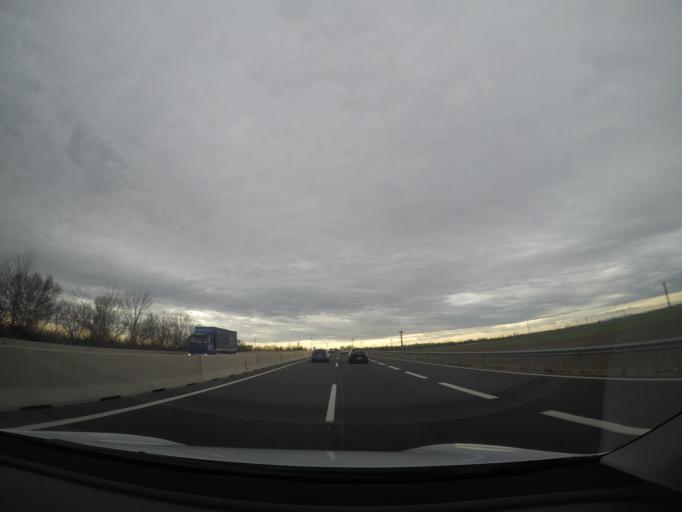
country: AT
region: Lower Austria
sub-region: Politischer Bezirk Modling
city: Munchendorf
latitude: 48.0180
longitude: 16.3595
